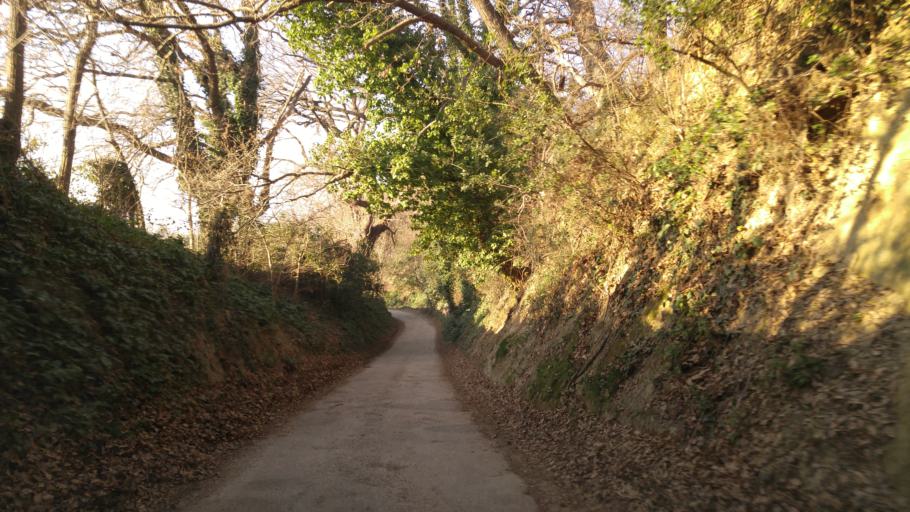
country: IT
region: The Marches
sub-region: Provincia di Pesaro e Urbino
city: Fenile
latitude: 43.8610
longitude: 12.9657
